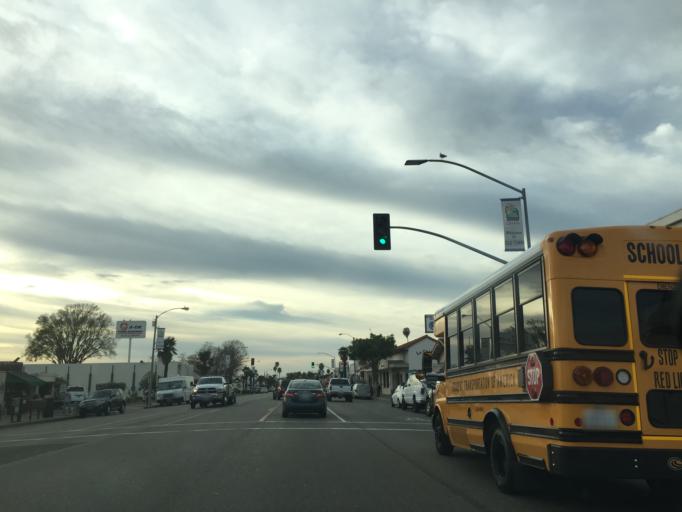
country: US
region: California
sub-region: Santa Barbara County
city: Goleta
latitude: 34.4358
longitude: -119.8250
